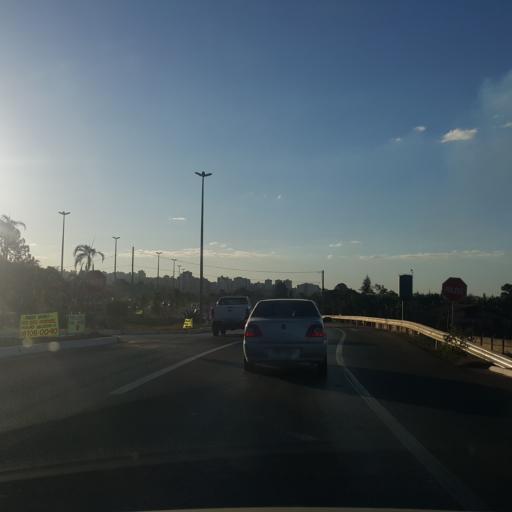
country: BR
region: Federal District
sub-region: Brasilia
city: Brasilia
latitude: -15.8551
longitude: -47.9920
